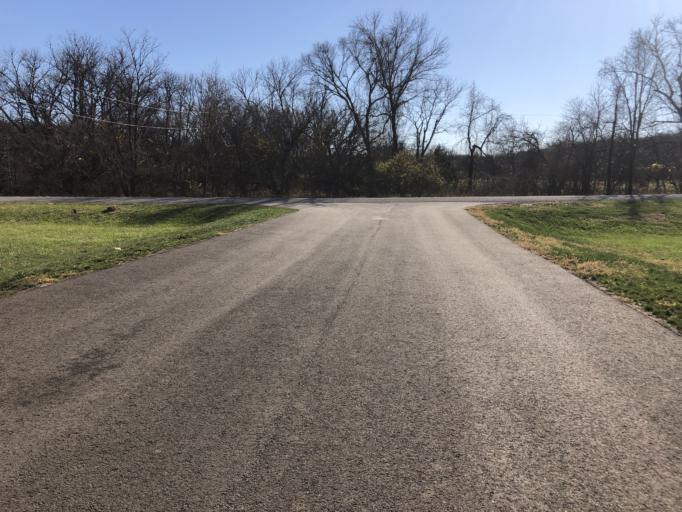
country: US
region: Kansas
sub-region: Johnson County
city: Gardner
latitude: 38.8697
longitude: -94.9496
